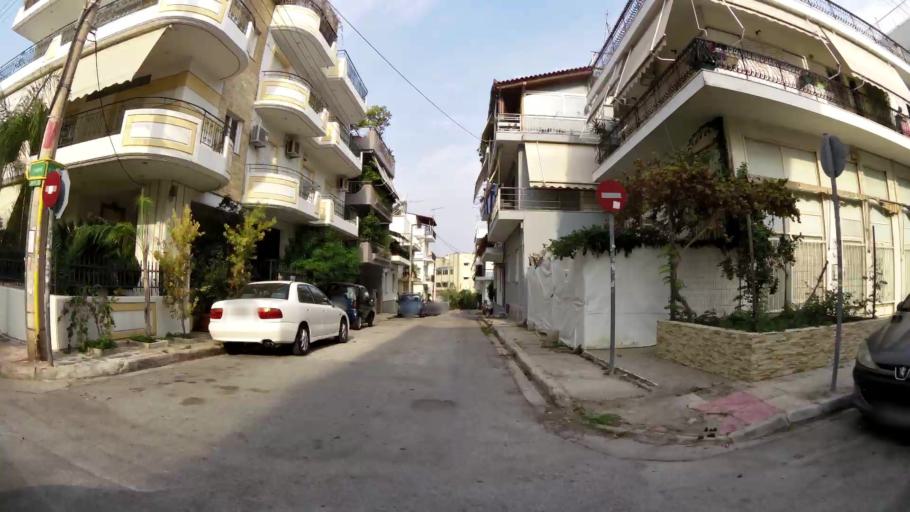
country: GR
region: Attica
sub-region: Nomarchia Athinas
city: Agios Dimitrios
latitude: 37.9268
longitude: 23.7204
